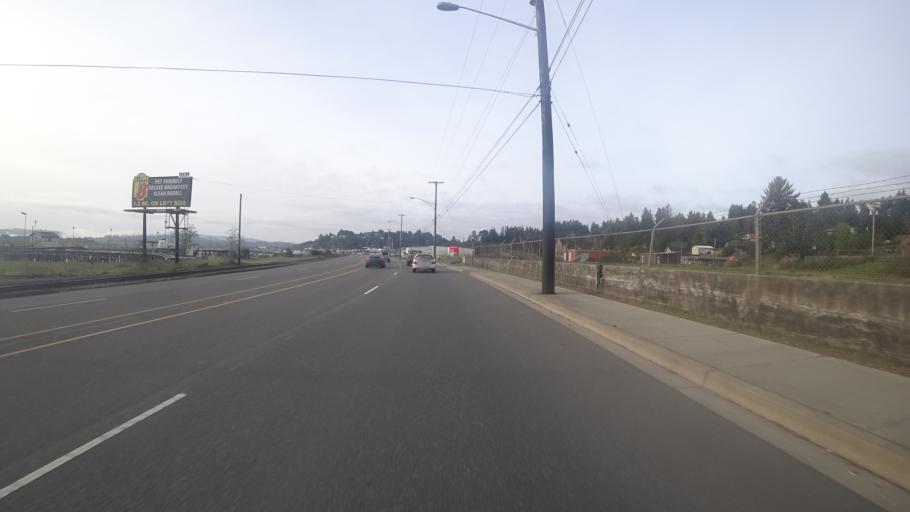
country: US
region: Oregon
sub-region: Coos County
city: Coos Bay
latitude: 43.3854
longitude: -124.2215
